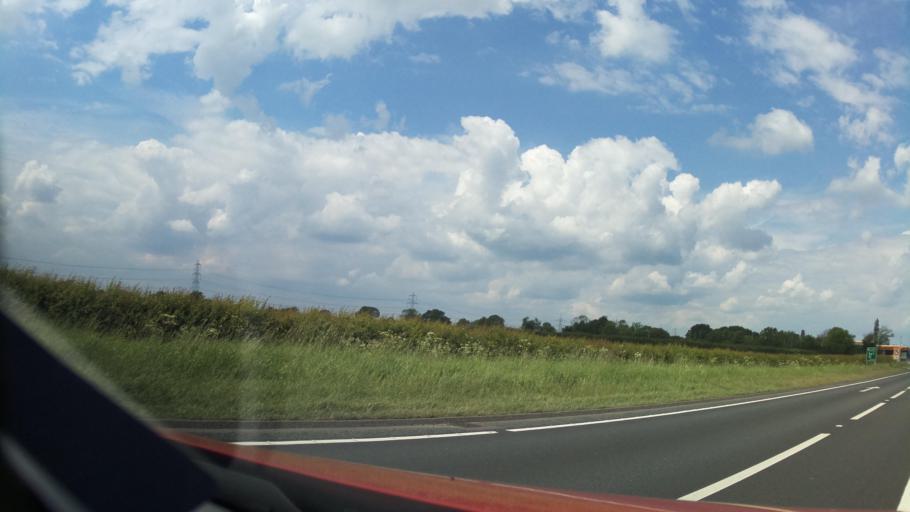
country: GB
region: England
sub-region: Stockton-on-Tees
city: Yarm
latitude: 54.4017
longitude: -1.3199
